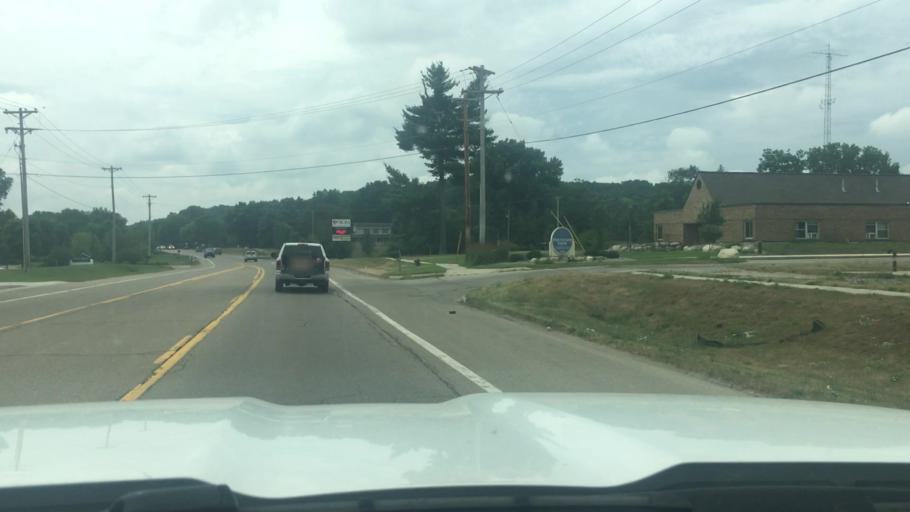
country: US
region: Michigan
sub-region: Kent County
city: Lowell
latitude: 42.9303
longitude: -85.3819
